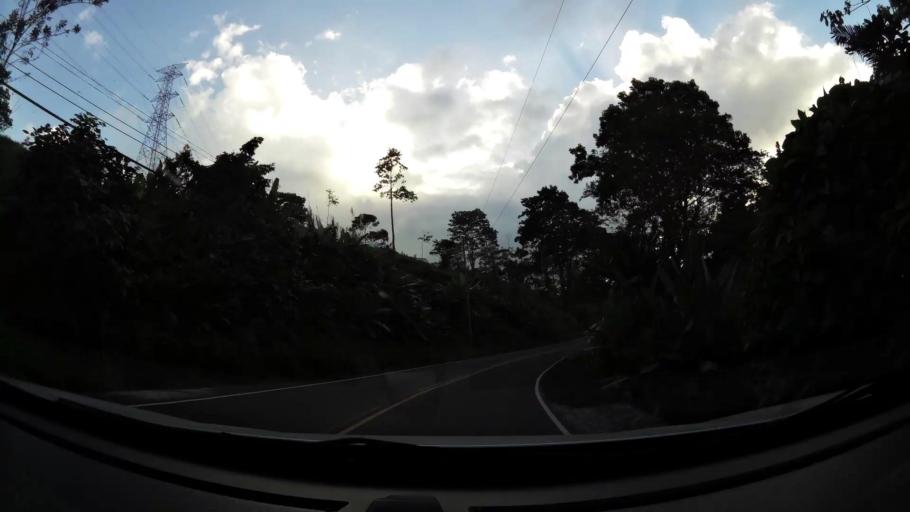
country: CR
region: Limon
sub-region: Canton de Siquirres
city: Siquirres
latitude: 10.0033
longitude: -83.5736
